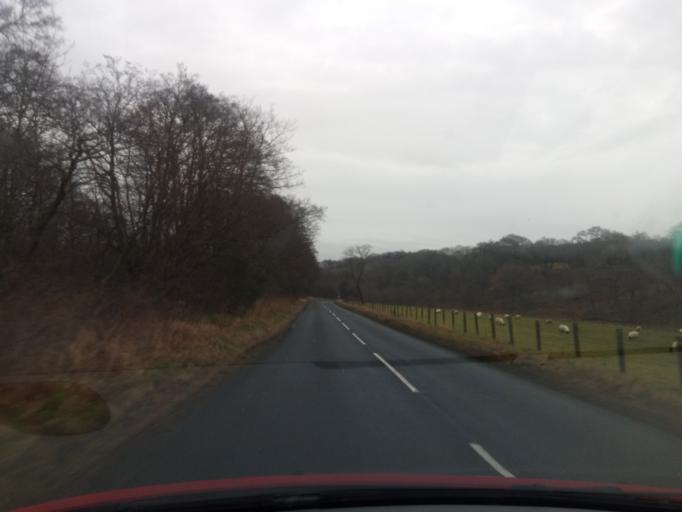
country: GB
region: England
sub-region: Northumberland
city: Rochester
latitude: 55.1663
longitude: -2.3892
